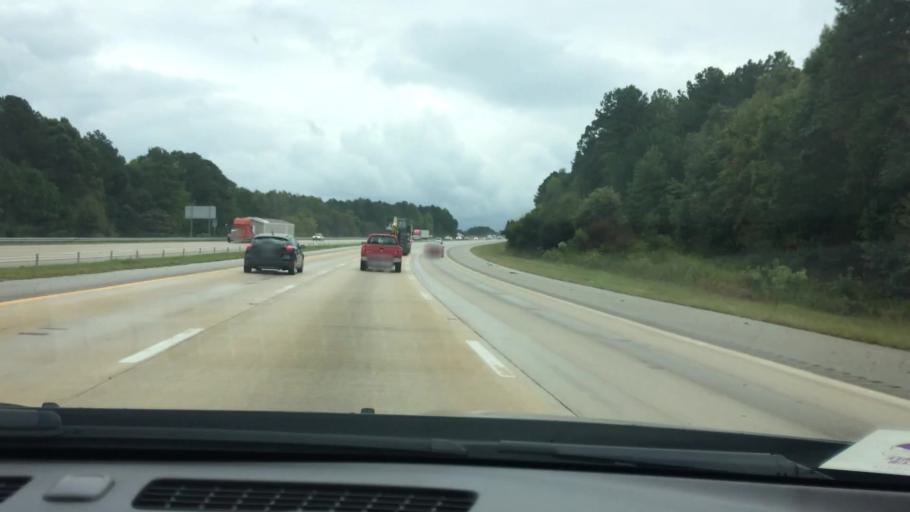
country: US
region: North Carolina
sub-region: Wake County
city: Knightdale
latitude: 35.7721
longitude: -78.5342
